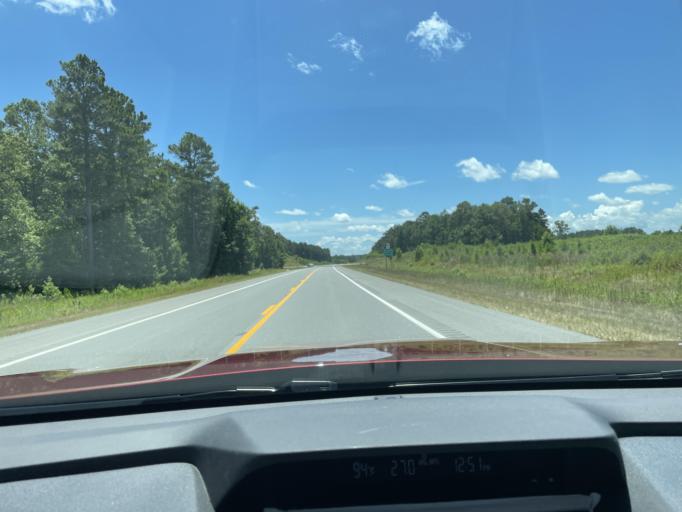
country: US
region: Arkansas
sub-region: Lincoln County
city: Star City
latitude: 33.9341
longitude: -91.8904
